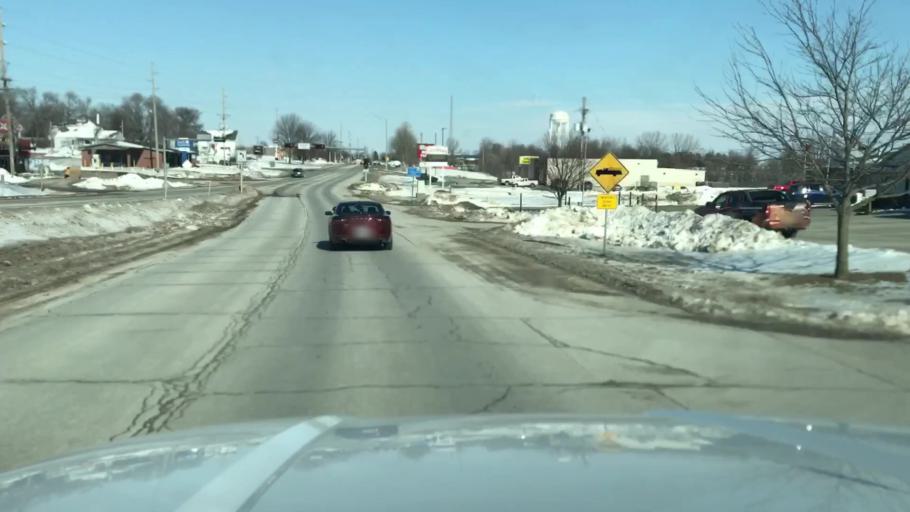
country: US
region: Missouri
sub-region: Andrew County
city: Savannah
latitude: 39.9397
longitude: -94.8217
